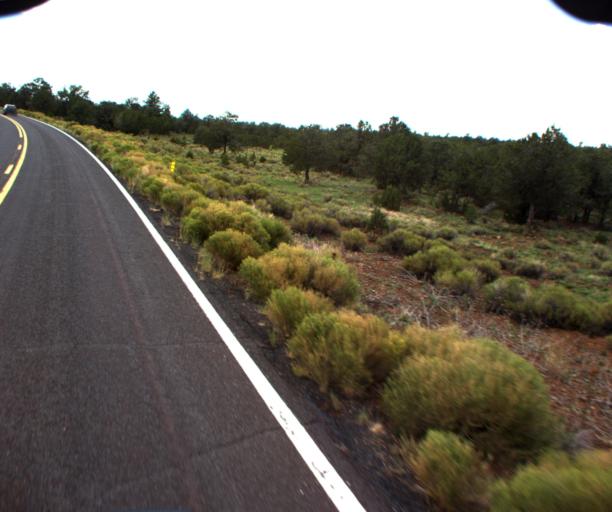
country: US
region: Arizona
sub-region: Coconino County
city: Parks
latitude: 35.5420
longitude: -111.8543
